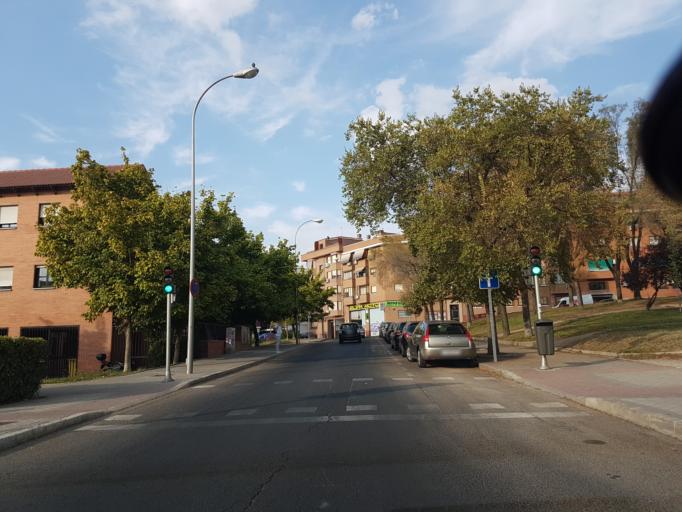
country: ES
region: Madrid
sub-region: Provincia de Madrid
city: Moratalaz
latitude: 40.4273
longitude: -3.6470
